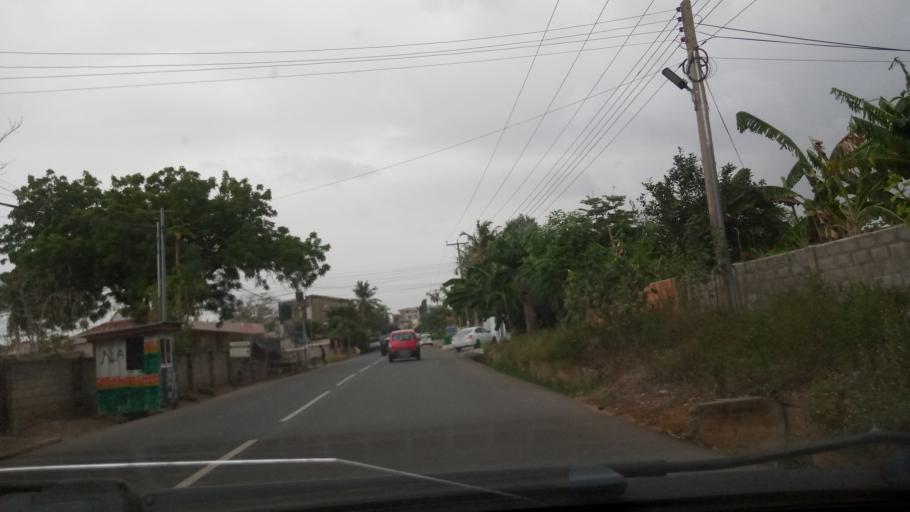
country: GH
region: Greater Accra
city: Dome
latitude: 5.6158
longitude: -0.1996
